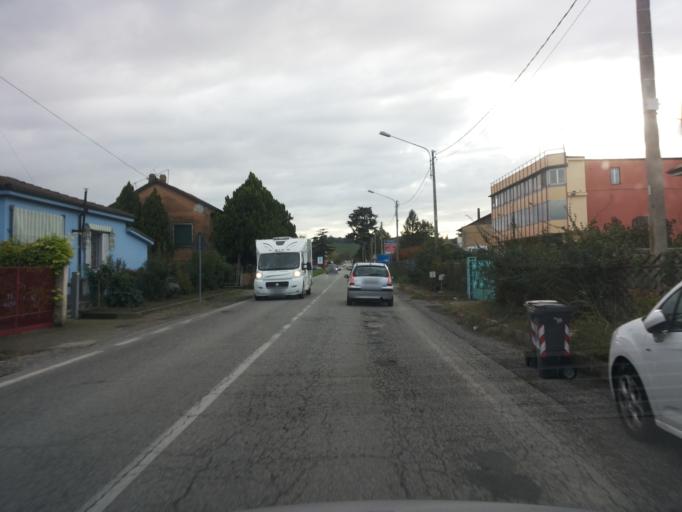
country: IT
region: Piedmont
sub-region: Provincia di Alessandria
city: San Giorgio Monferrato
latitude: 45.1056
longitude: 8.4358
